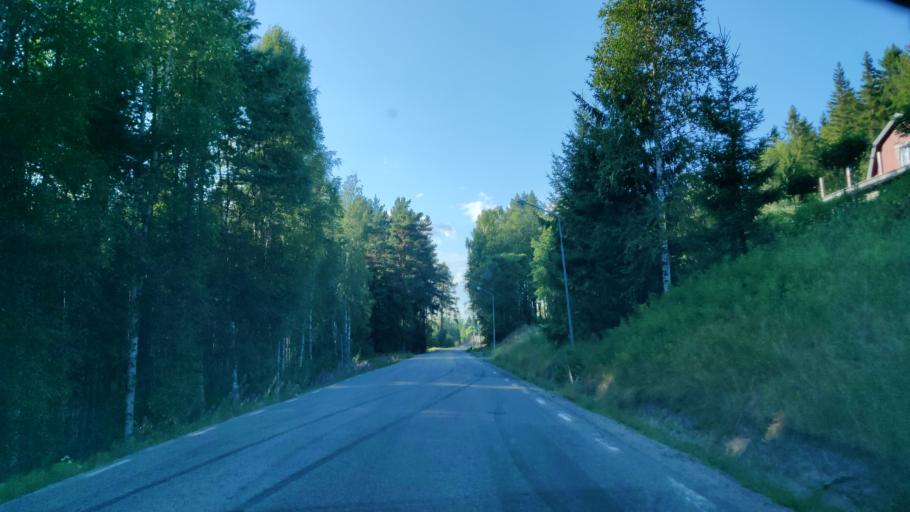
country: SE
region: Vaermland
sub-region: Hagfors Kommun
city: Ekshaerad
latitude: 60.1776
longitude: 13.5276
